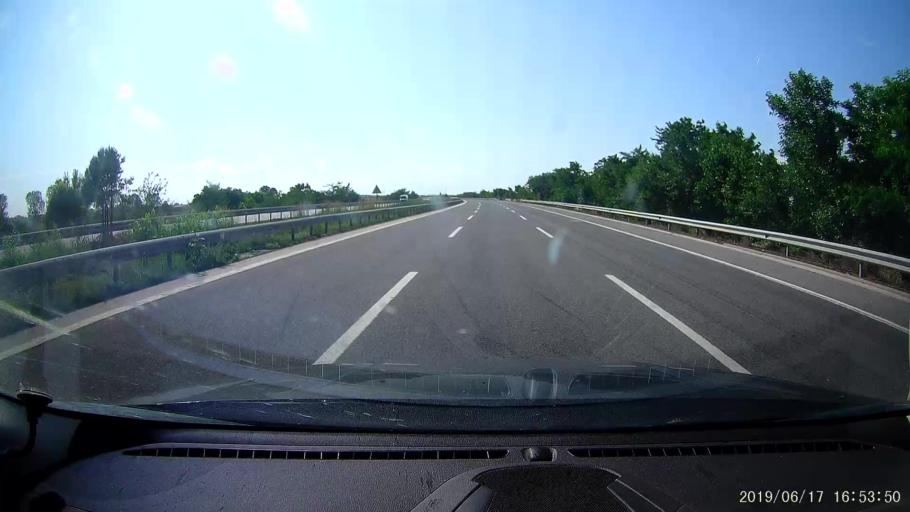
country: TR
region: Kirklareli
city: Inece
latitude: 41.5685
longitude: 27.0130
